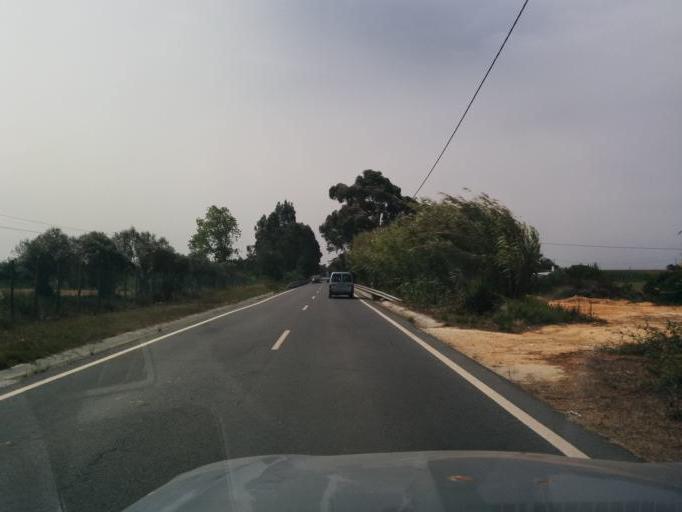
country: PT
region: Beja
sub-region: Odemira
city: Vila Nova de Milfontes
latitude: 37.6522
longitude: -8.7595
